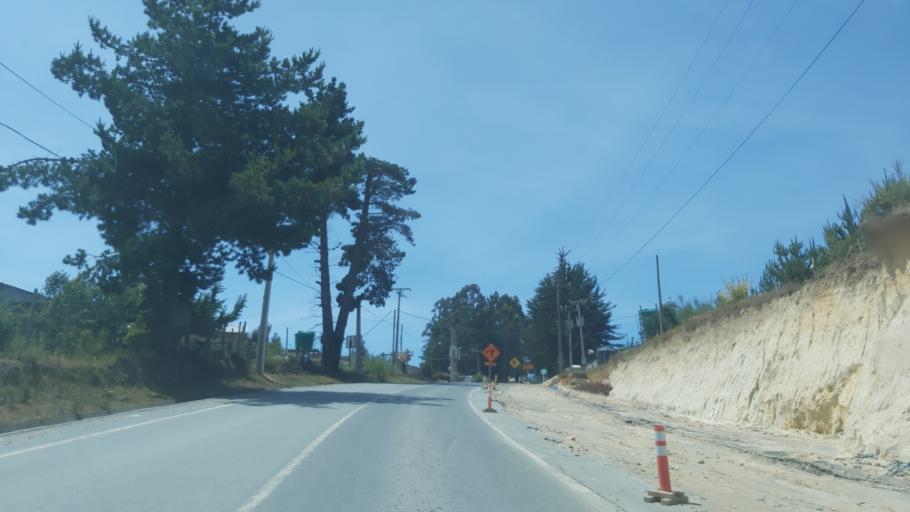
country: CL
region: Maule
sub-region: Provincia de Talca
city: Constitucion
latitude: -35.4419
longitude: -72.4580
